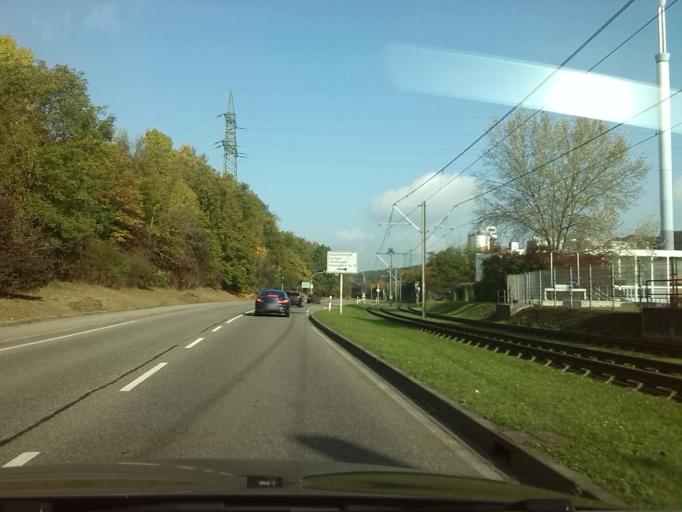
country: DE
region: Baden-Wuerttemberg
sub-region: Regierungsbezirk Stuttgart
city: Stuttgart Muehlhausen
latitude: 48.8473
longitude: 9.2403
